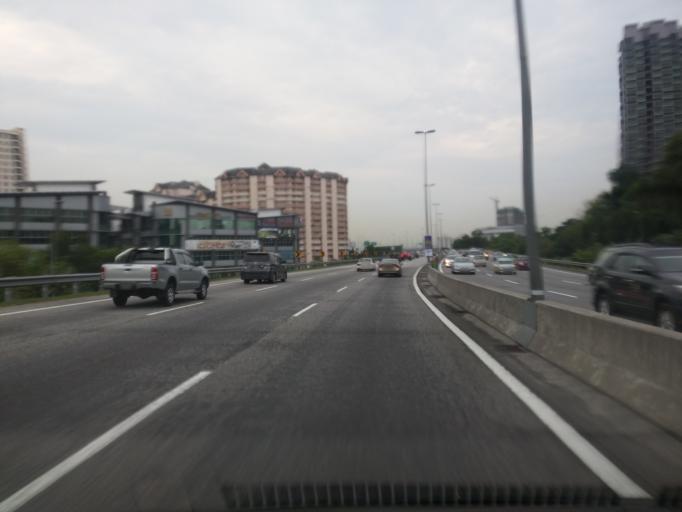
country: MY
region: Kuala Lumpur
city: Kuala Lumpur
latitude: 3.0840
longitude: 101.6927
